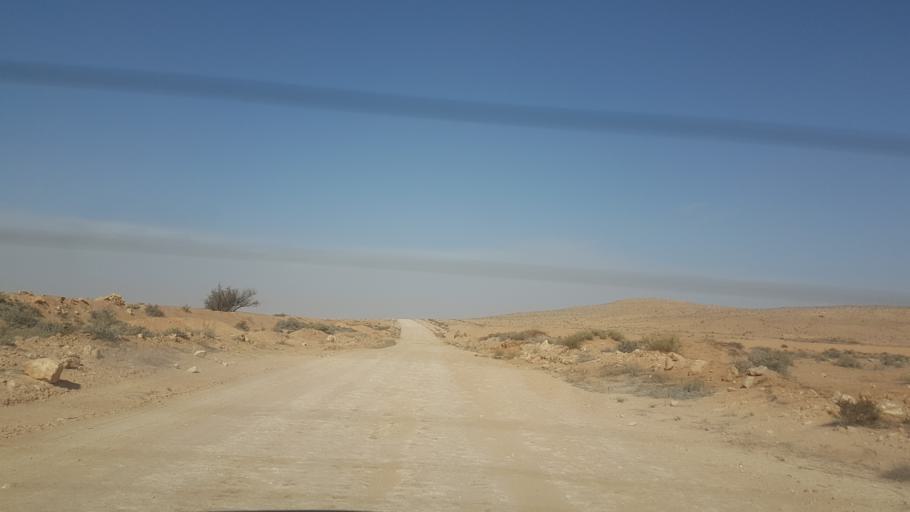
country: TN
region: Qabis
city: El Hamma
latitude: 33.6536
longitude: 9.7359
